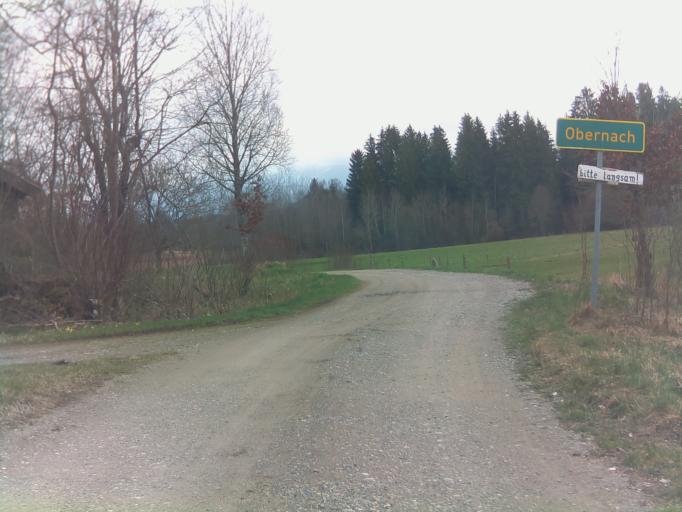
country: DE
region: Bavaria
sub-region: Upper Bavaria
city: Uffing
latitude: 47.6927
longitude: 11.1161
